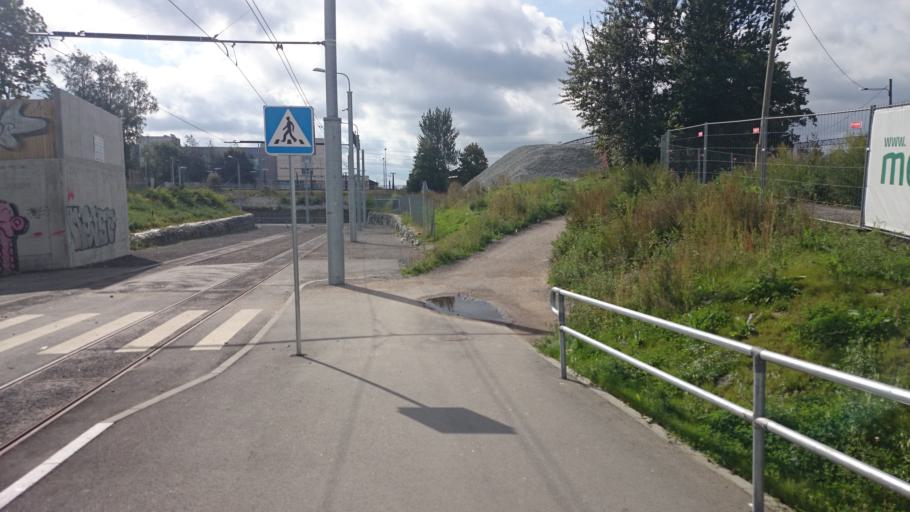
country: EE
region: Harju
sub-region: Tallinna linn
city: Tallinn
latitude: 59.4247
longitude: 24.7968
